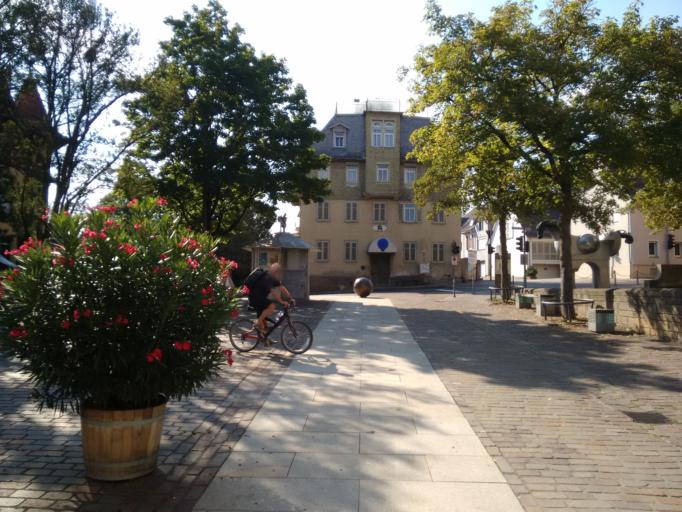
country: DE
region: Baden-Wuerttemberg
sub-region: Regierungsbezirk Stuttgart
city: Bietigheim-Bissingen
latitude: 48.9596
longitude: 9.1237
